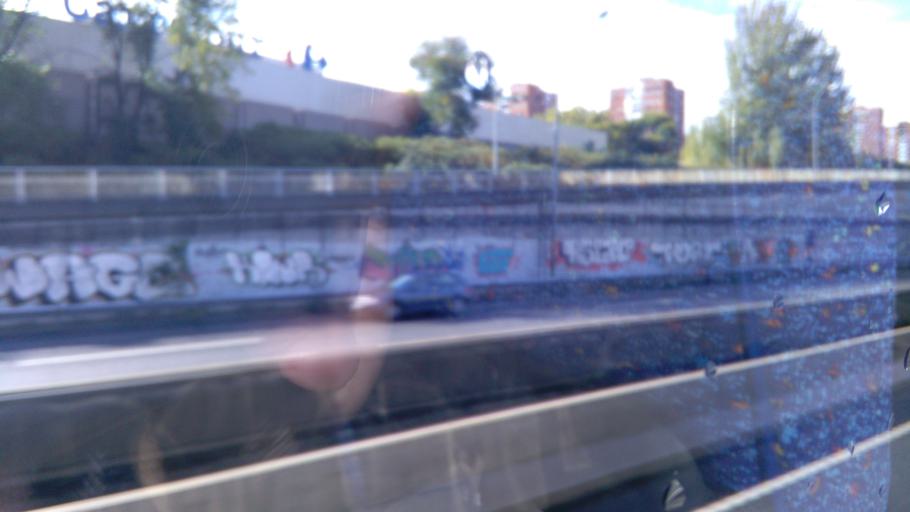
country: ES
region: Madrid
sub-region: Provincia de Madrid
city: Villaverde
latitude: 40.3644
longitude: -3.6919
